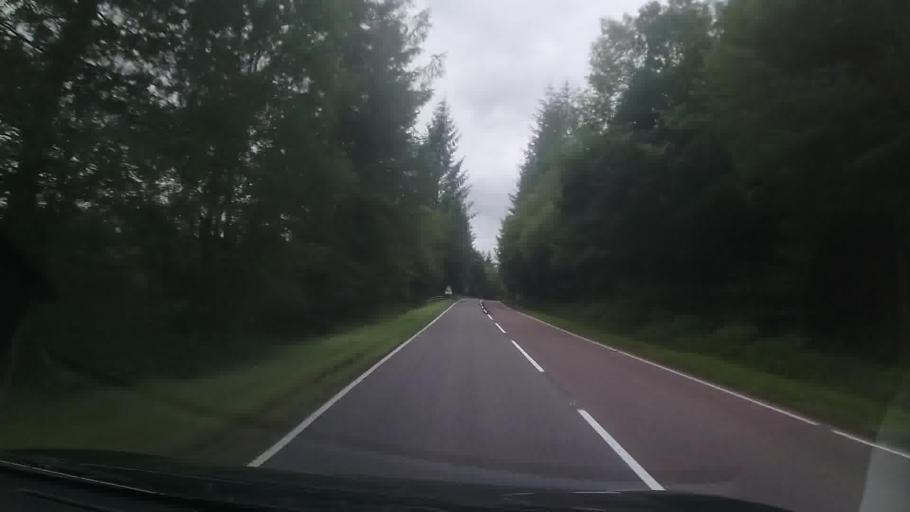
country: GB
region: Scotland
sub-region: Argyll and Bute
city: Garelochhead
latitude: 56.2564
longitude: -5.0904
